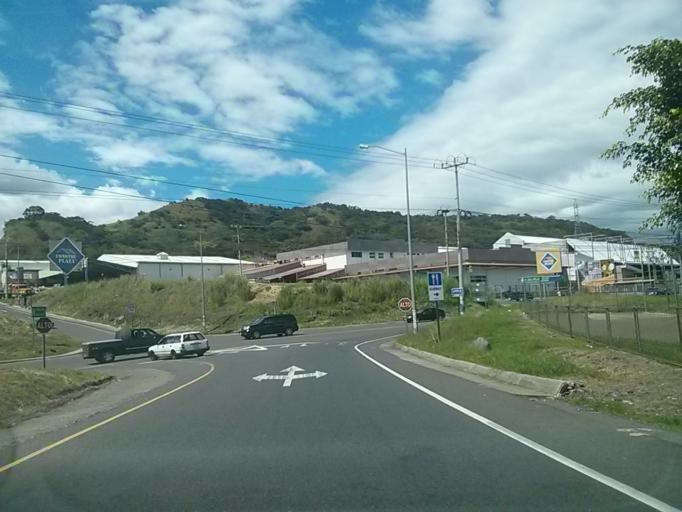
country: CR
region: San Jose
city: Santa Ana
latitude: 9.9476
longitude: -84.1615
